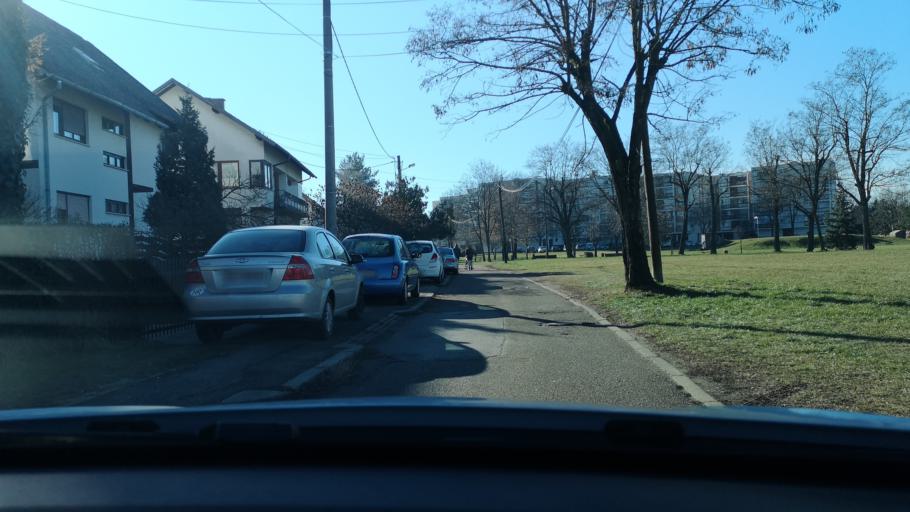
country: HR
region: Zagrebacka
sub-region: Grad Velika Gorica
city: Velika Gorica
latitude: 45.7208
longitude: 16.0634
